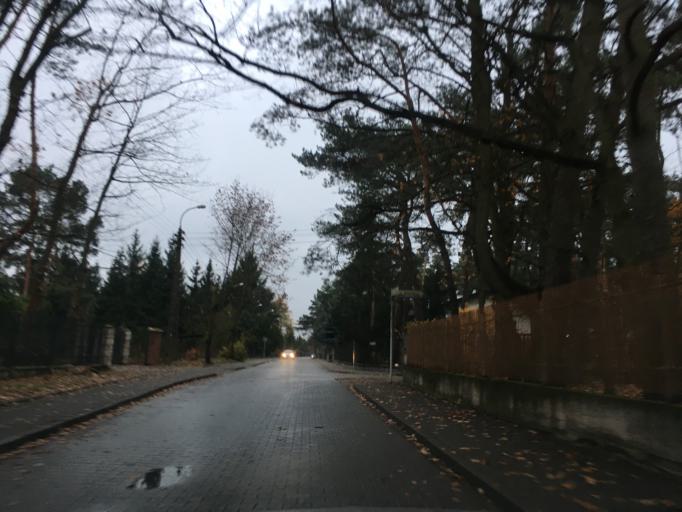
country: PL
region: Masovian Voivodeship
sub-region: Powiat piaseczynski
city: Lesznowola
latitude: 52.0906
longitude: 20.8937
